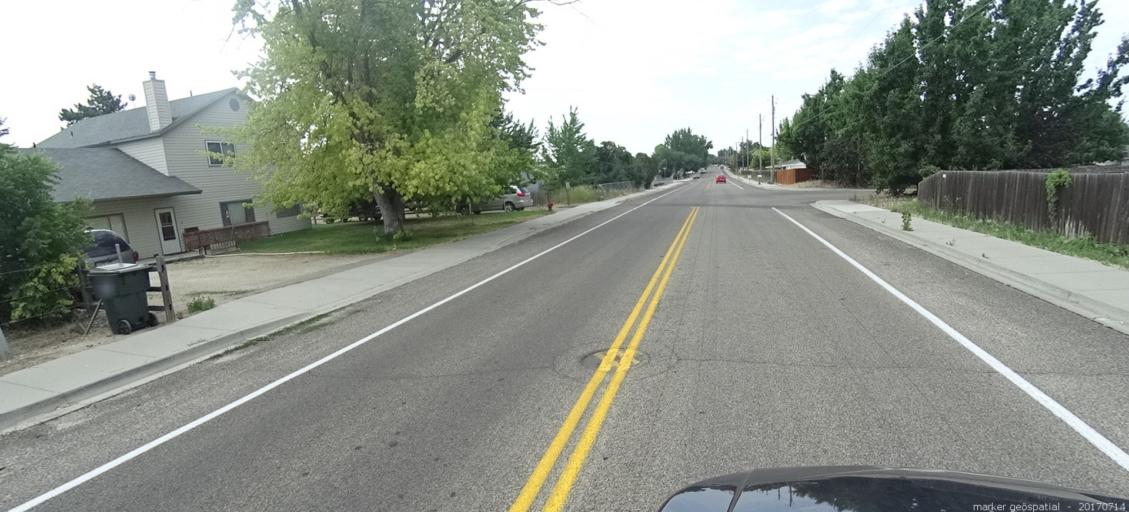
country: US
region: Idaho
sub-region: Ada County
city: Kuna
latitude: 43.4994
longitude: -116.4236
